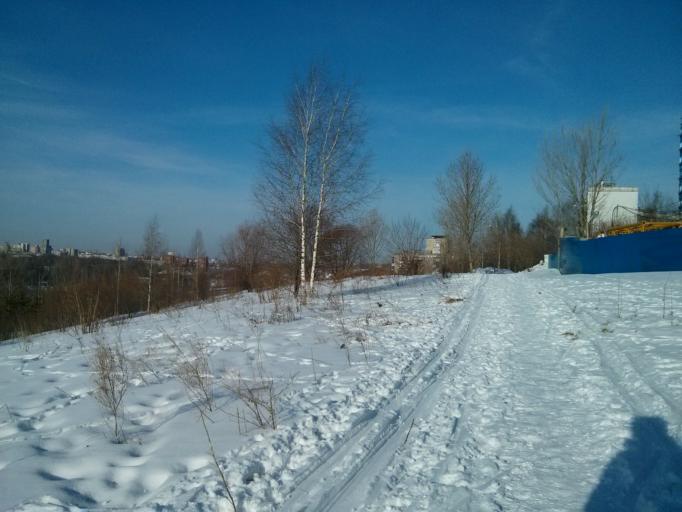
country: RU
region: Nizjnij Novgorod
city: Afonino
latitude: 56.2928
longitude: 44.0590
